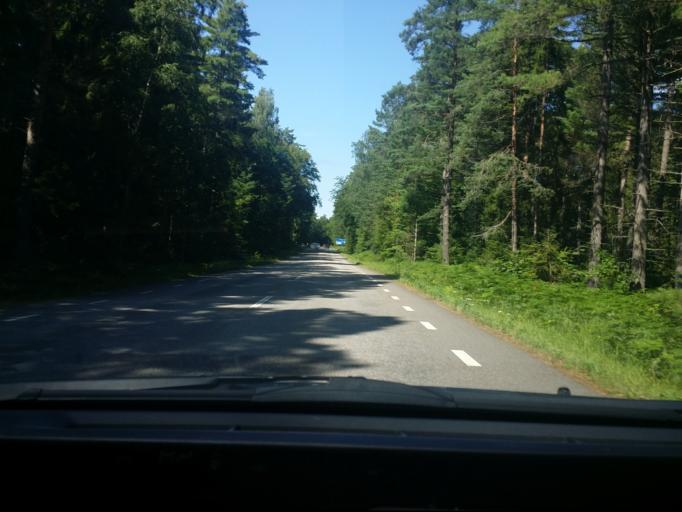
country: SE
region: Kalmar
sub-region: Borgholms Kommun
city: Borgholm
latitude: 57.2732
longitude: 17.0242
